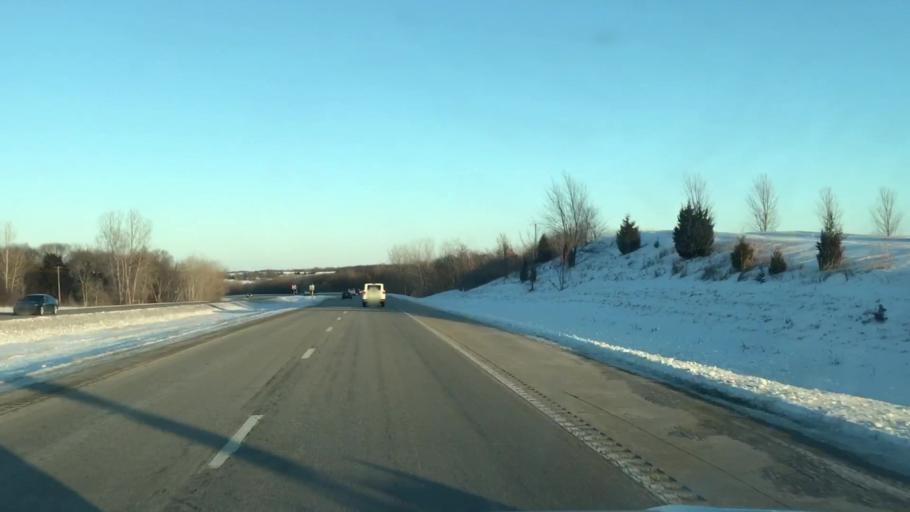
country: US
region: Missouri
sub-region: Clinton County
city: Gower
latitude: 39.7469
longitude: -94.6109
